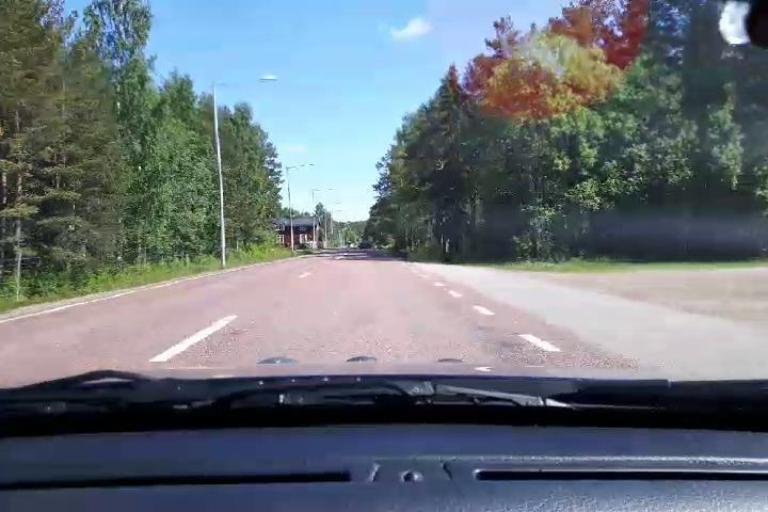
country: SE
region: Gaevleborg
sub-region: Hudiksvalls Kommun
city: Delsbo
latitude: 61.7877
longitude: 16.6072
